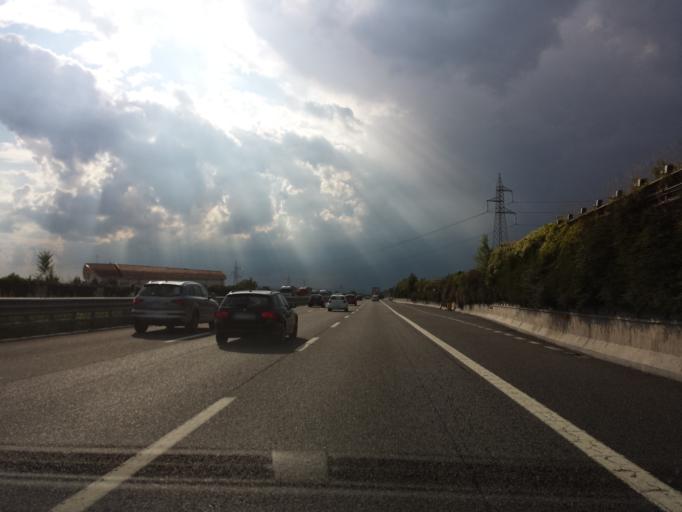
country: IT
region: Veneto
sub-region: Provincia di Padova
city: Villaguattera
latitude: 45.4509
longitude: 11.8305
